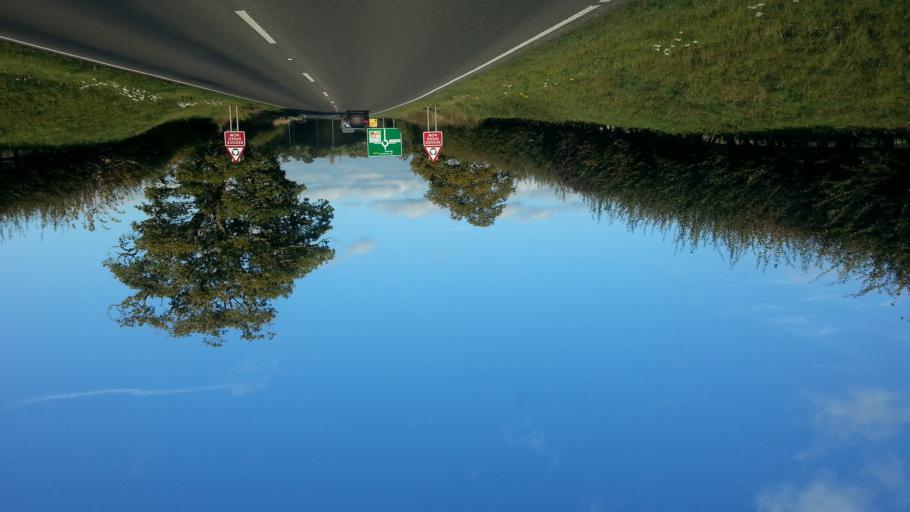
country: GB
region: England
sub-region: Norfolk
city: Harleston
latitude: 52.4081
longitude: 1.3177
